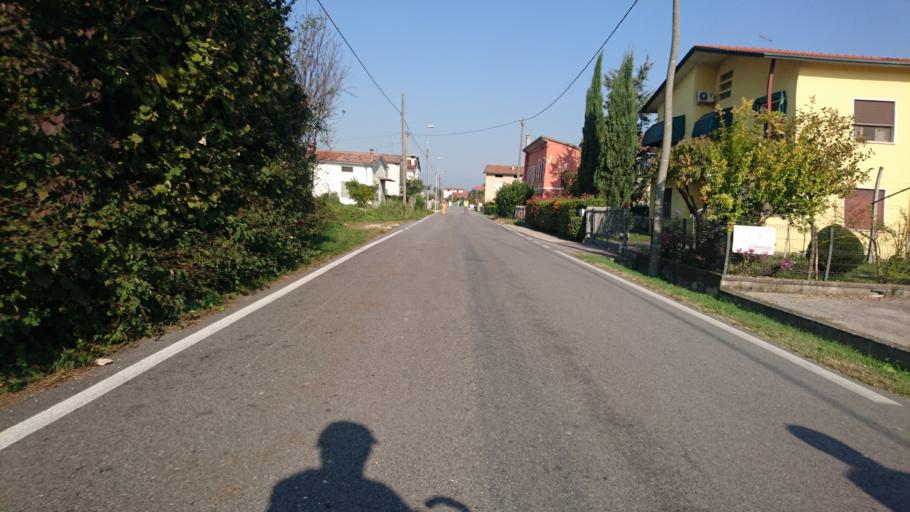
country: IT
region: Veneto
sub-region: Provincia di Padova
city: San Pietro in Gu
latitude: 45.6001
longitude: 11.6908
